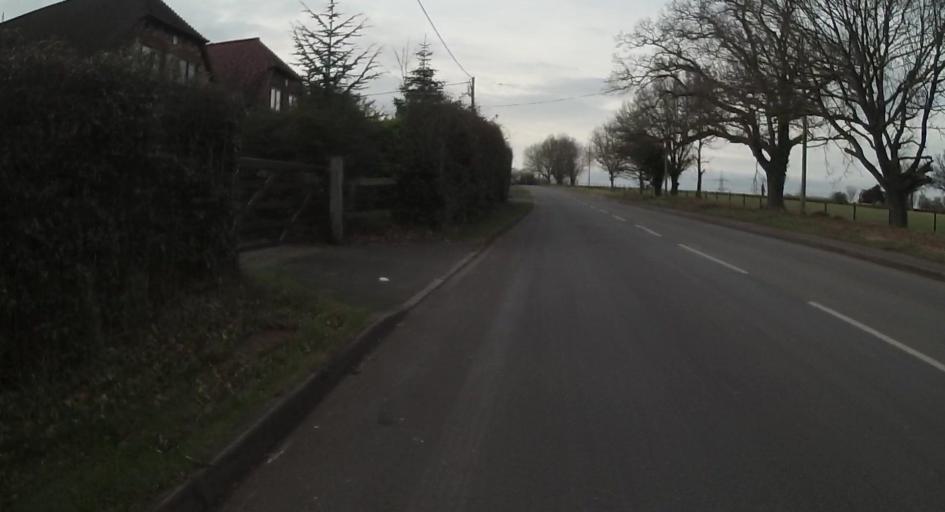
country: GB
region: England
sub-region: West Berkshire
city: Calcot
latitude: 51.4156
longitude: -1.0541
